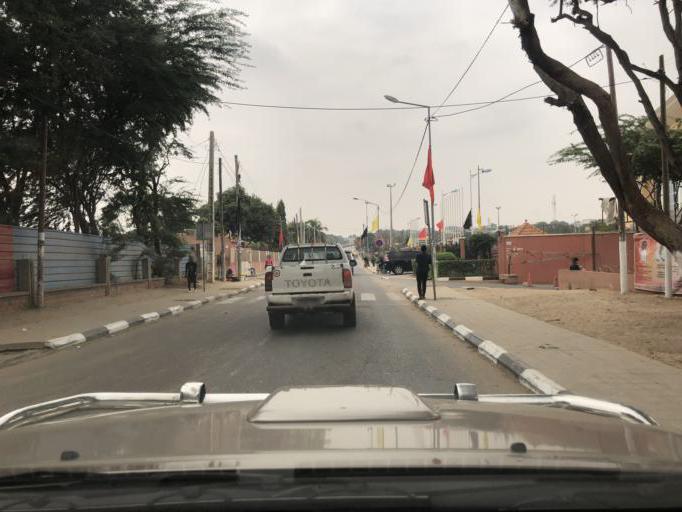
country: AO
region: Luanda
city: Luanda
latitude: -8.9083
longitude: 13.1640
